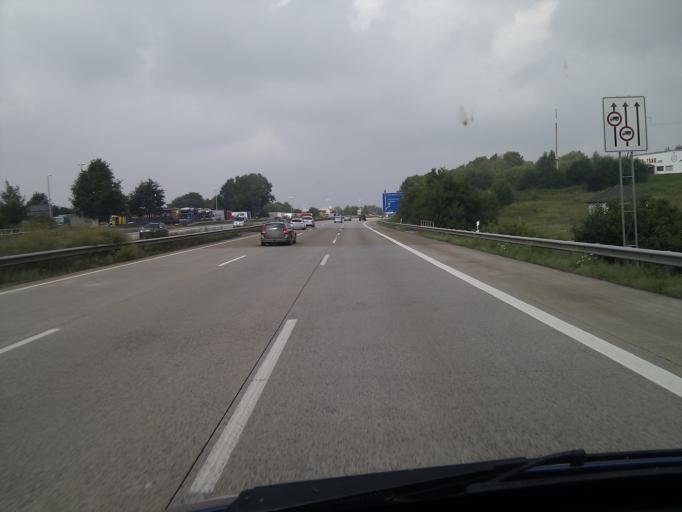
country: DE
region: Rheinland-Pfalz
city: Breitscheid
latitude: 50.5978
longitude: 7.4394
